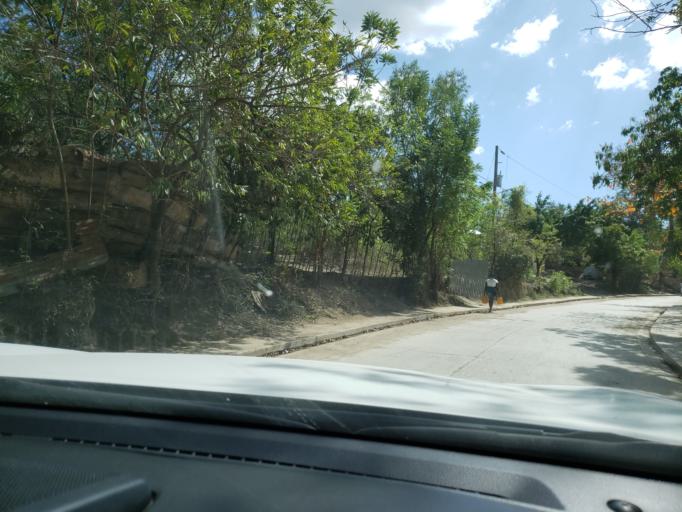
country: HT
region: Grandans
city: Anse-a-Veau
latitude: 18.4529
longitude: -73.3797
